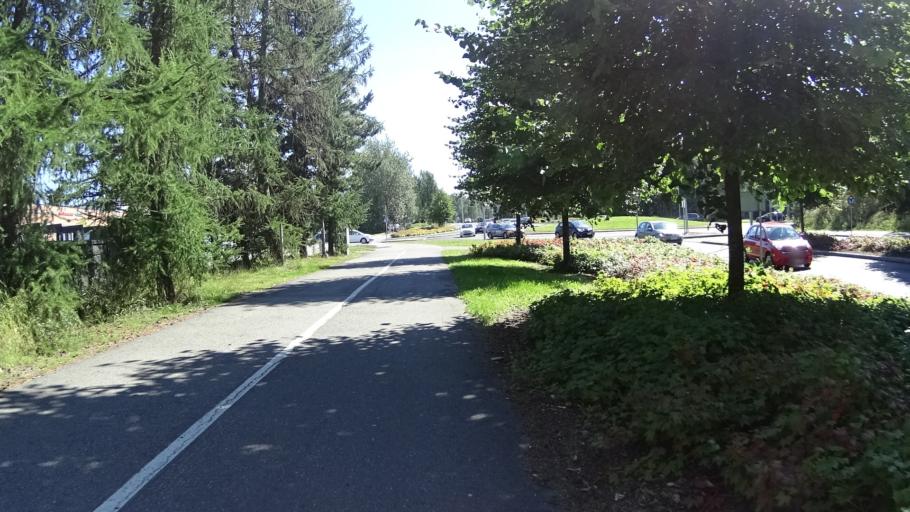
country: FI
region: Uusimaa
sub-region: Helsinki
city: Teekkarikylae
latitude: 60.2368
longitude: 24.8890
